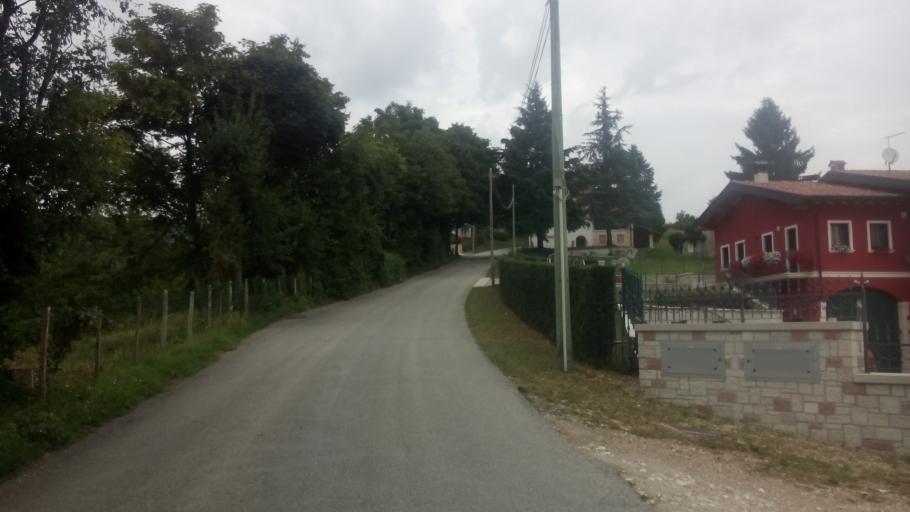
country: IT
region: Veneto
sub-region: Provincia di Vicenza
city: Conco
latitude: 45.7927
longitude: 11.6043
